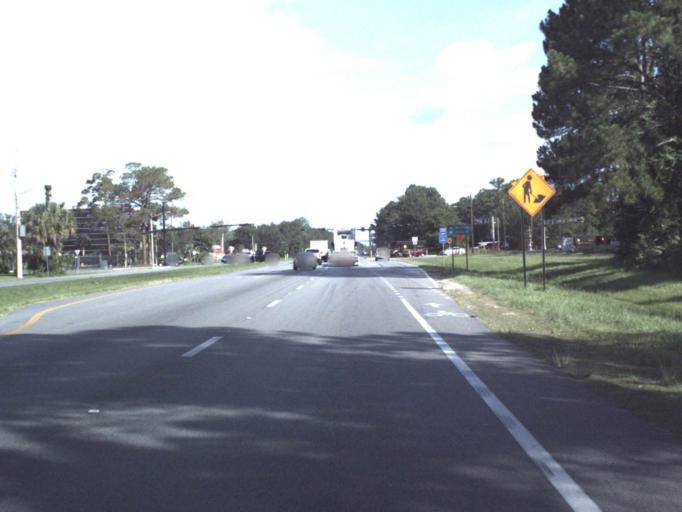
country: US
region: Florida
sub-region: Alachua County
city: Gainesville
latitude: 29.7108
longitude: -82.3523
